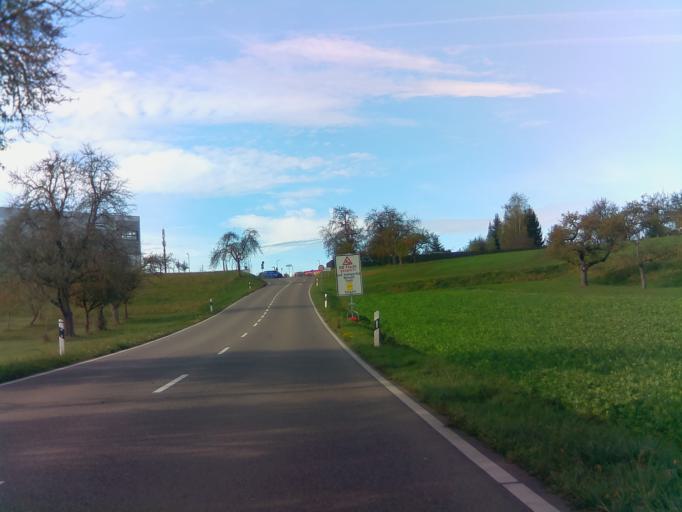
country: DE
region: Baden-Wuerttemberg
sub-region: Regierungsbezirk Stuttgart
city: Rutesheim
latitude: 48.8105
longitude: 8.9318
